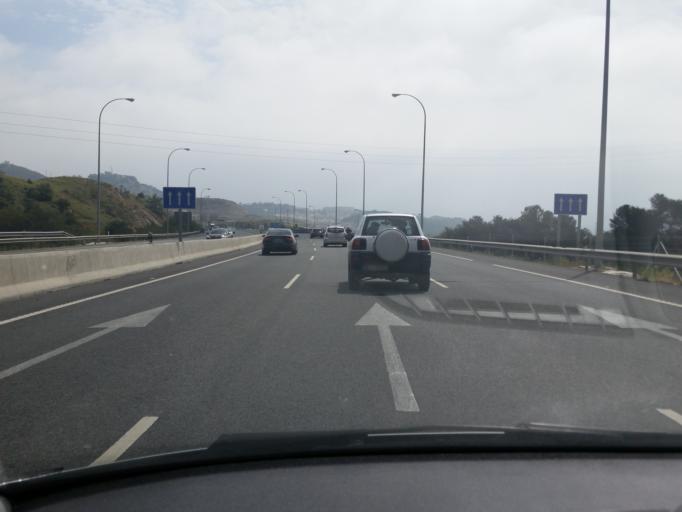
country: ES
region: Andalusia
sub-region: Provincia de Malaga
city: Malaga
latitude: 36.7441
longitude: -4.4068
